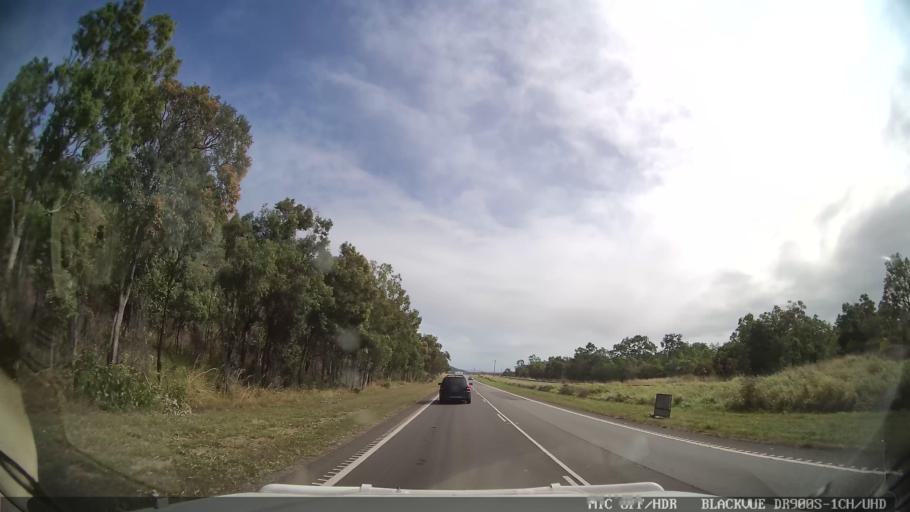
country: AU
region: Queensland
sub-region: Townsville
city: Townsville
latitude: -19.4021
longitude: 147.0259
